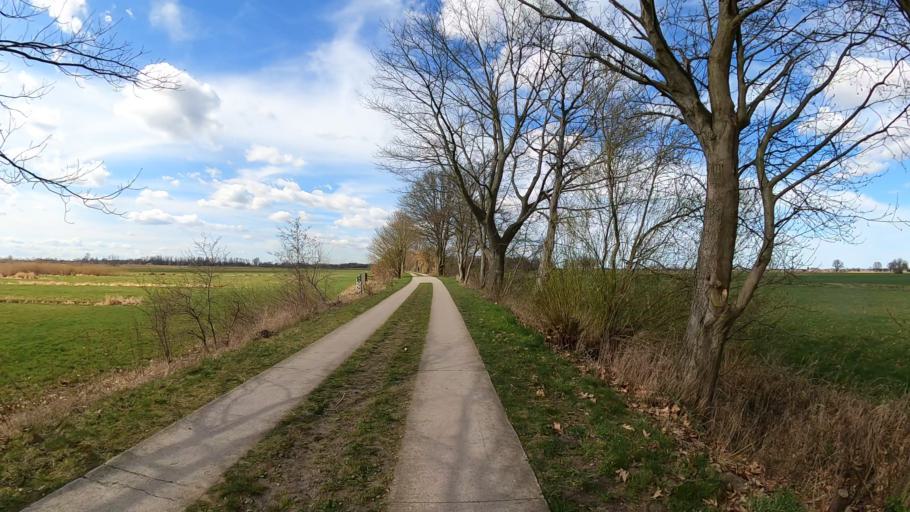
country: DE
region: Lower Saxony
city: Winsen
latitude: 53.4160
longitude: 10.1811
